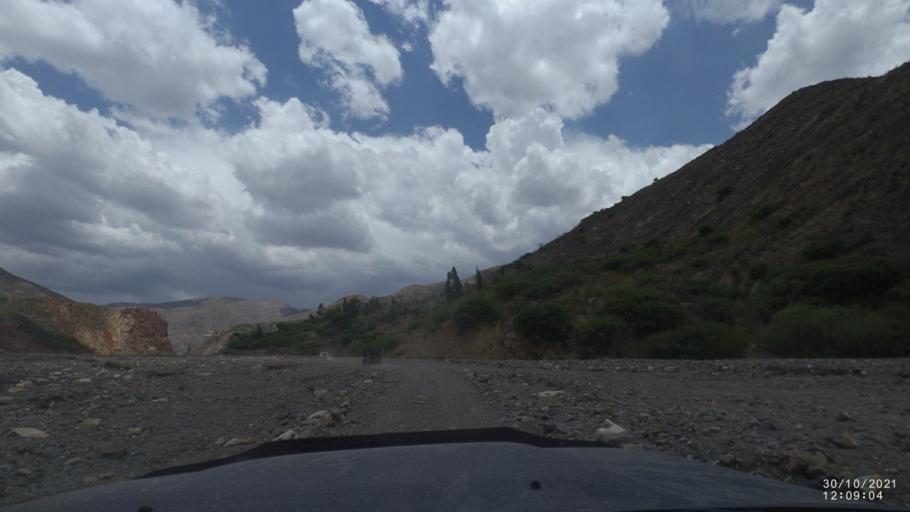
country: BO
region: Cochabamba
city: Colchani
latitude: -17.5446
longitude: -66.6275
